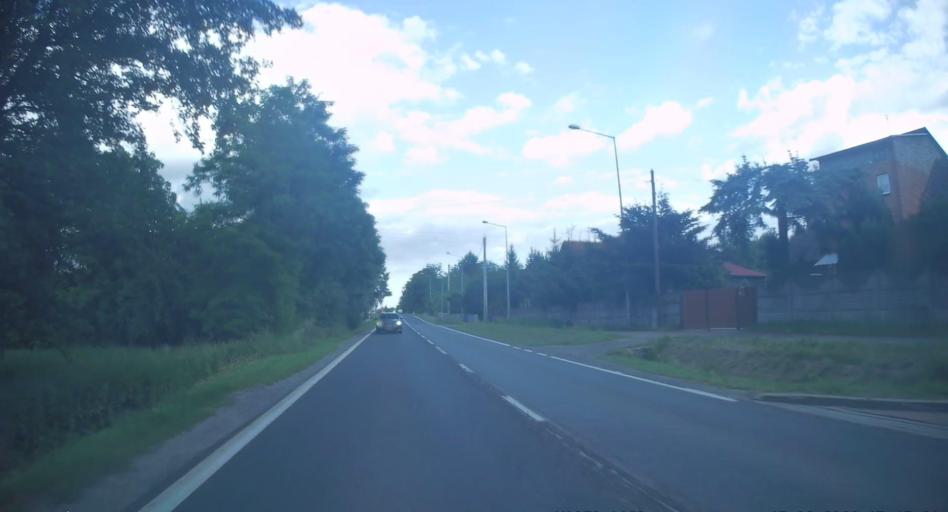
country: PL
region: Silesian Voivodeship
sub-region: Powiat bielski
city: Czaniec
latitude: 49.8805
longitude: 19.2543
